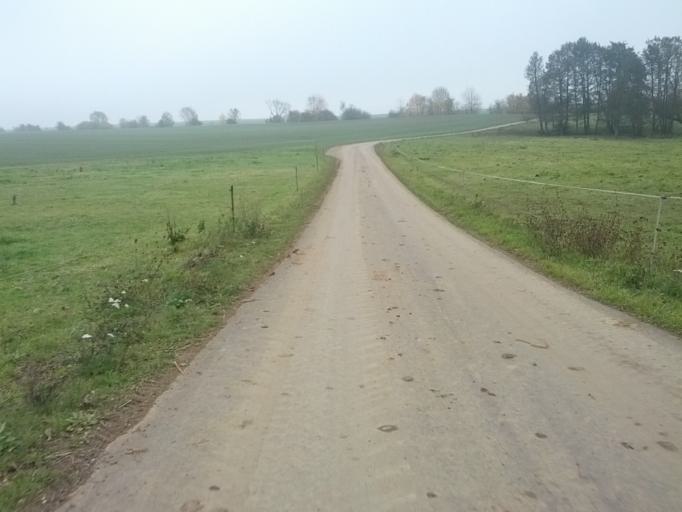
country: DE
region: Thuringia
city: Bischofroda
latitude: 50.9881
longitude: 10.3923
